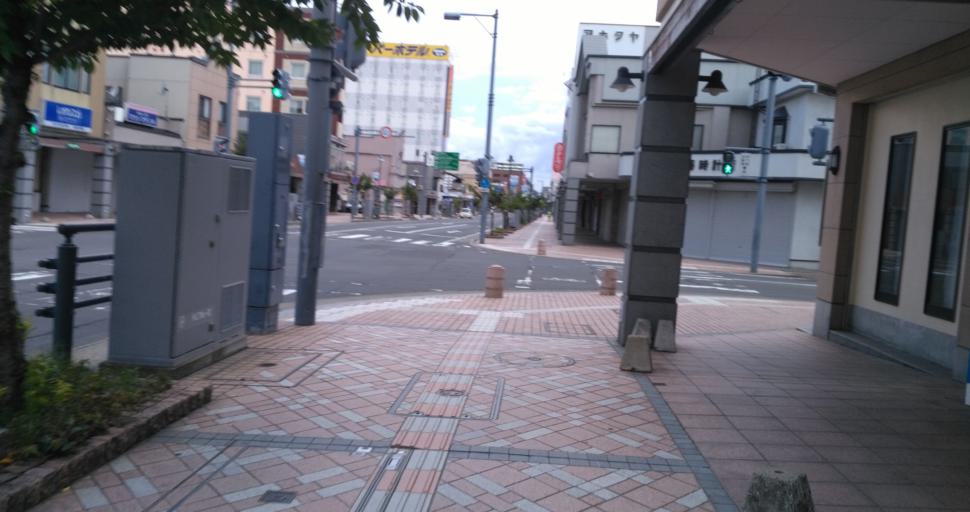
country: JP
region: Aomori
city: Hirosaki
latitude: 40.5966
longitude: 140.4775
